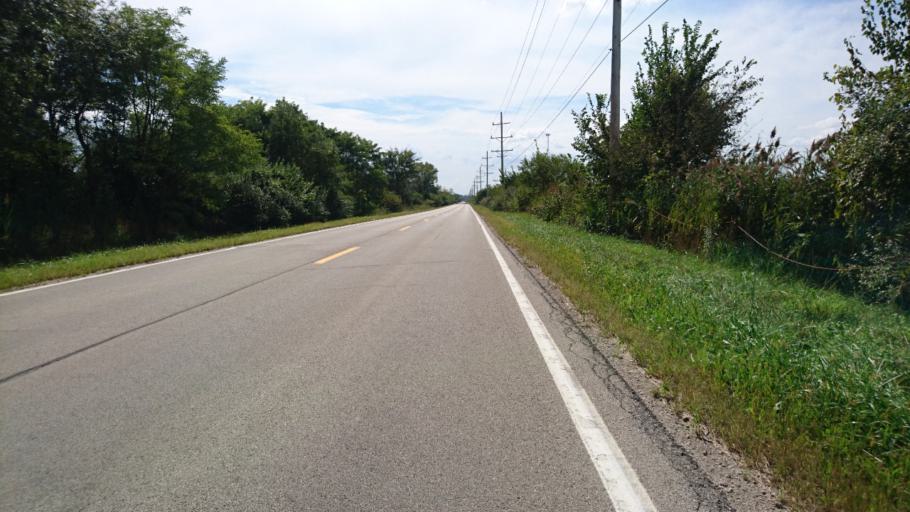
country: US
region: Illinois
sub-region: Grundy County
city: Central City
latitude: 41.2191
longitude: -88.2684
